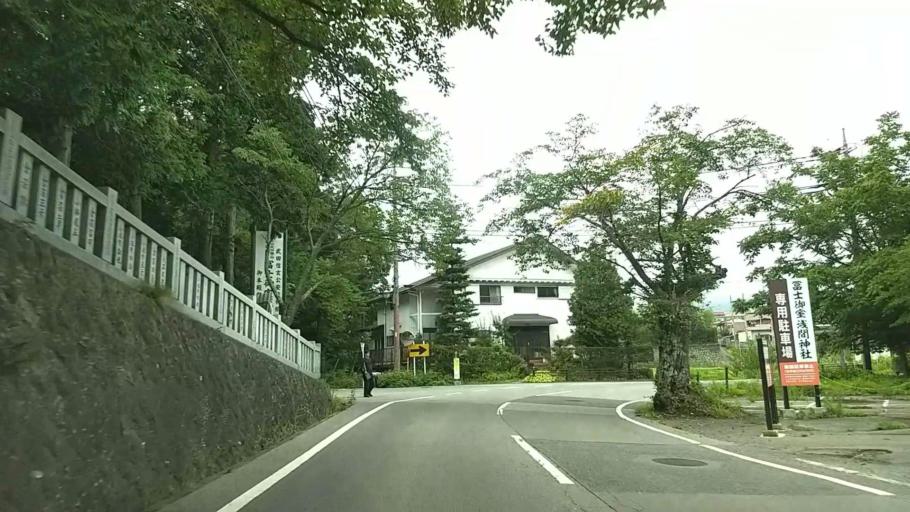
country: JP
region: Yamanashi
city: Fujikawaguchiko
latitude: 35.5101
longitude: 138.7450
